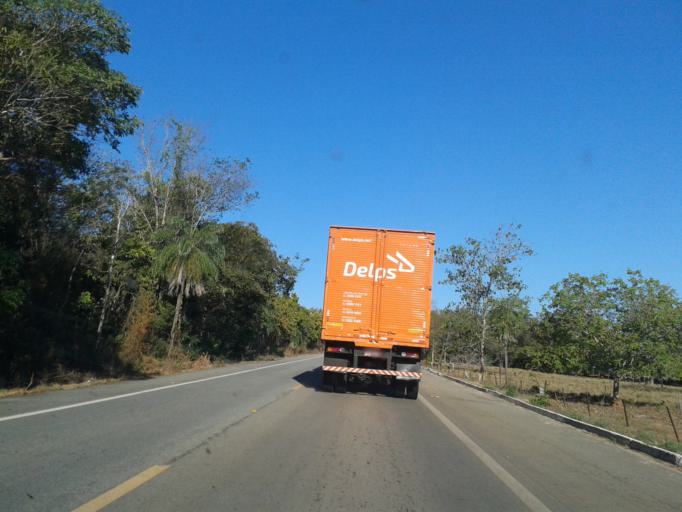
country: BR
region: Goias
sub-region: Itapirapua
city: Itapirapua
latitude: -15.3196
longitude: -50.4375
